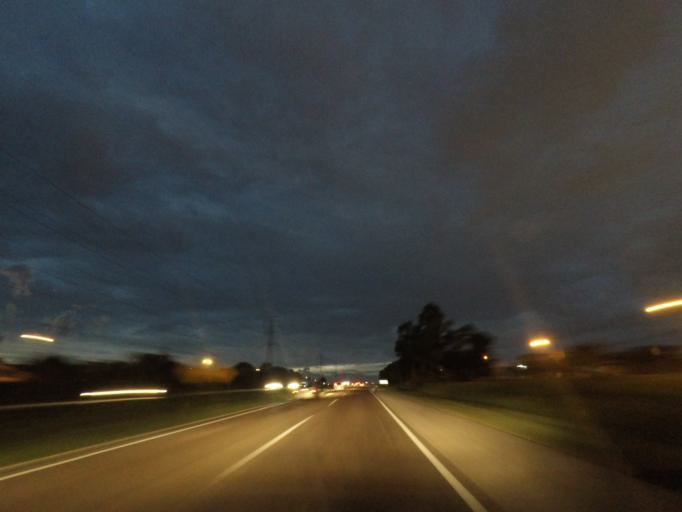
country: BR
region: Parana
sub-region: Curitiba
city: Curitiba
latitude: -25.4890
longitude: -49.3454
